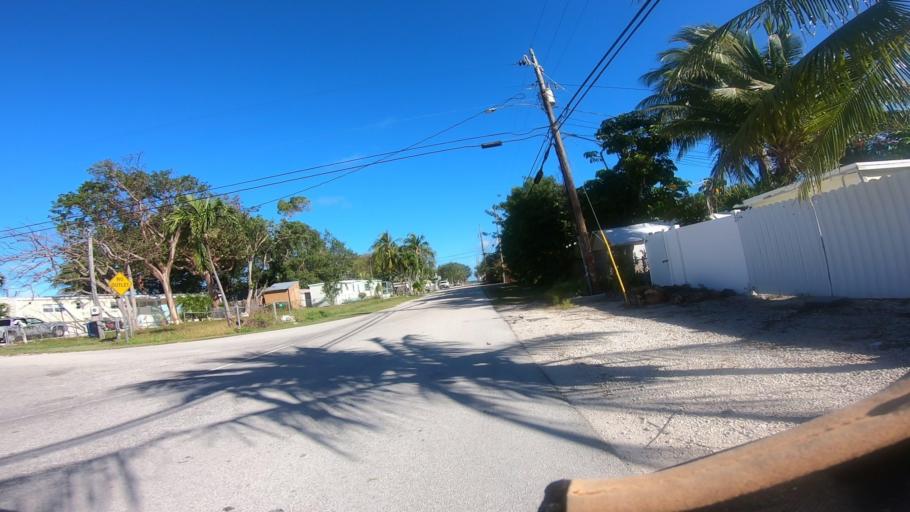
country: US
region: Florida
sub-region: Monroe County
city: Key Largo
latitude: 25.1121
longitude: -80.4257
